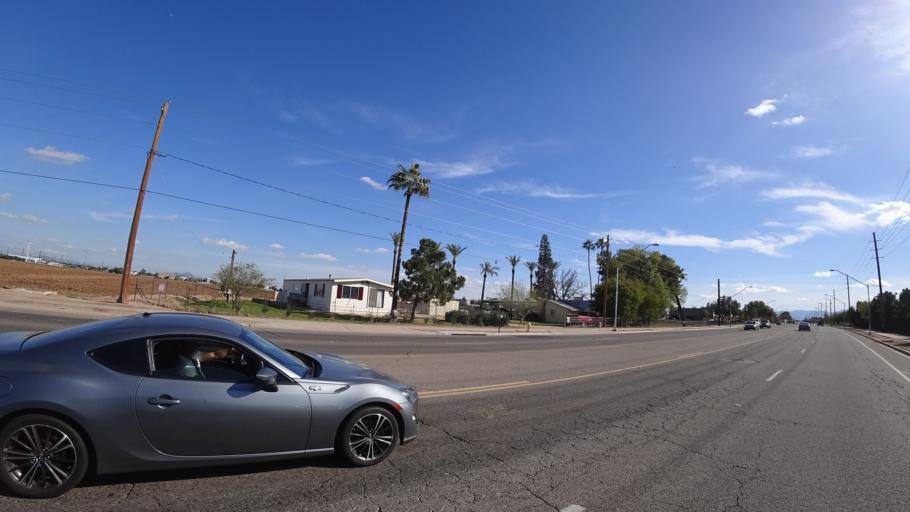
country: US
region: Arizona
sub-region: Maricopa County
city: Peoria
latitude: 33.5507
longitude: -112.2205
